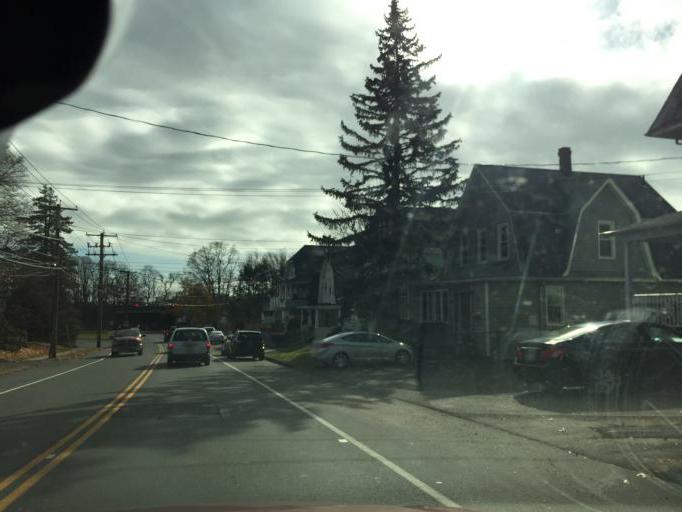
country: US
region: Connecticut
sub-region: Fairfield County
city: Bridgeport
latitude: 41.1668
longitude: -73.2364
